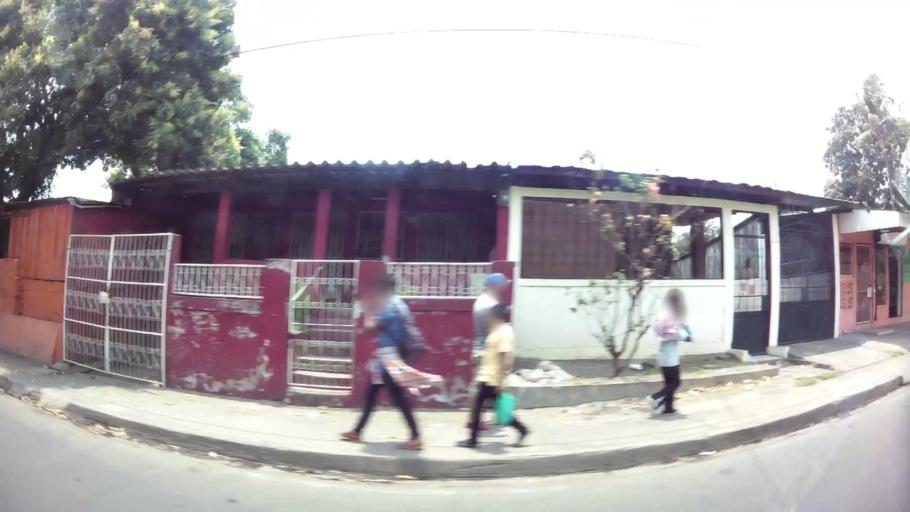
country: NI
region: Managua
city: Managua
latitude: 12.1122
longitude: -86.2980
